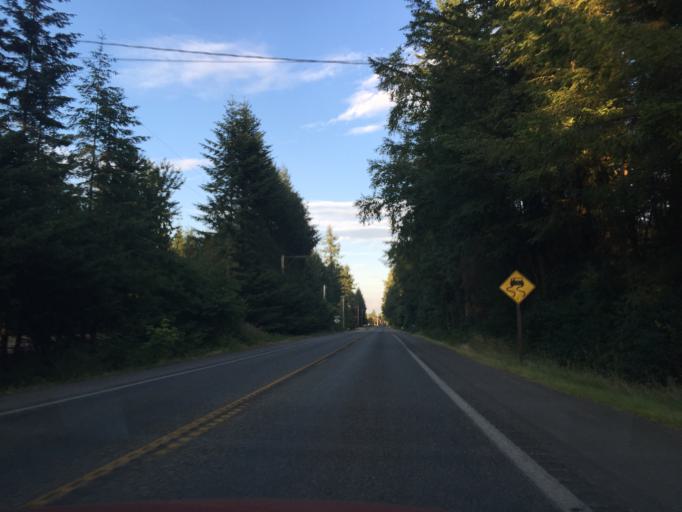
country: US
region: Washington
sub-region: Whatcom County
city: Ferndale
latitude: 48.9353
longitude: -122.6379
